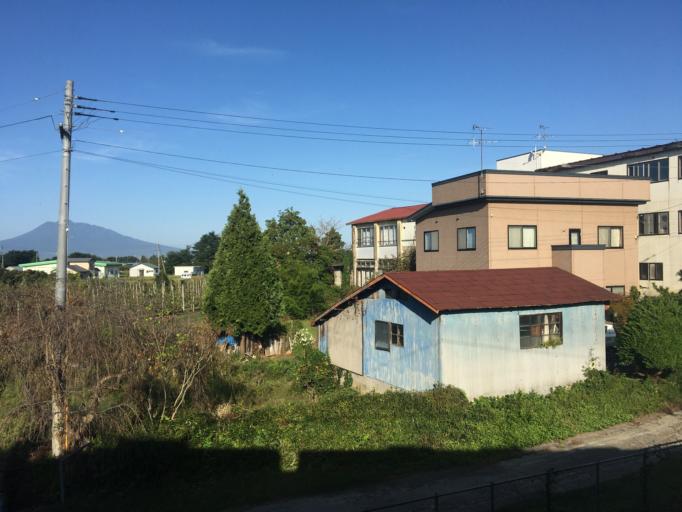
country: JP
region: Aomori
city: Kuroishi
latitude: 40.6490
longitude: 140.5759
